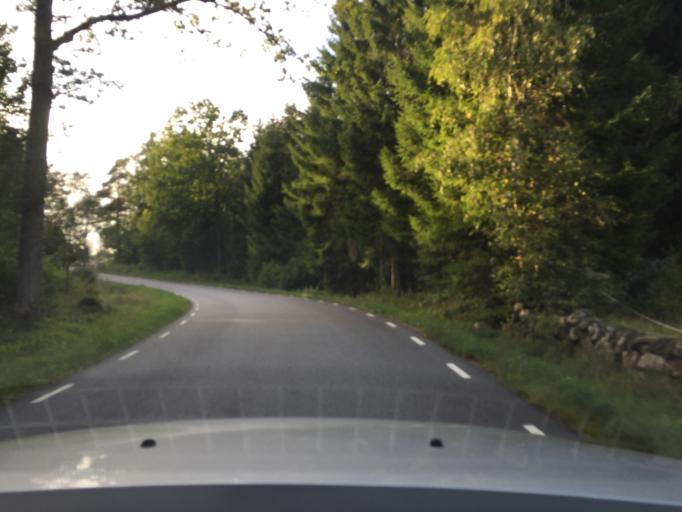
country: SE
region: Skane
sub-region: Hassleholms Kommun
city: Sosdala
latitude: 56.0564
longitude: 13.6038
